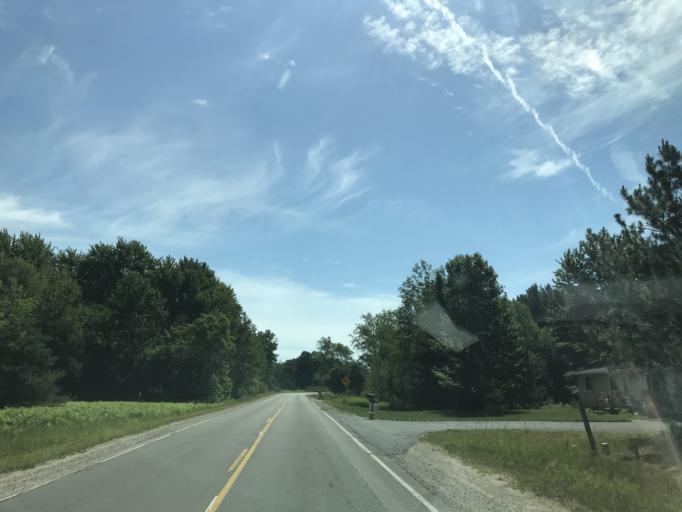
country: US
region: Michigan
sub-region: Grand Traverse County
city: Traverse City
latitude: 44.6582
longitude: -85.7208
